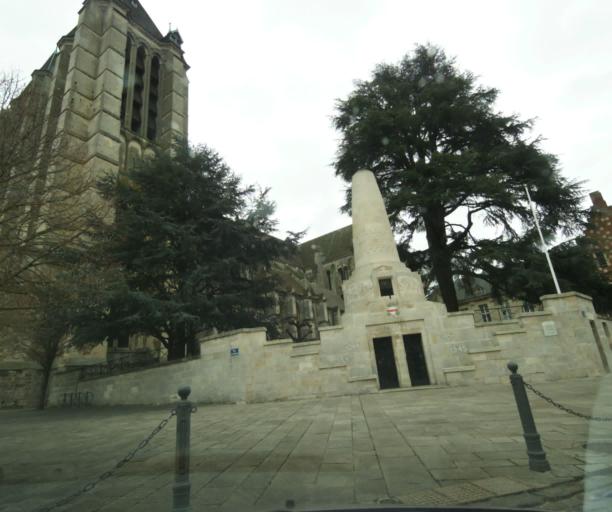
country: FR
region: Picardie
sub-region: Departement de l'Oise
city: Noyon
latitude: 49.5819
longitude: 2.9997
